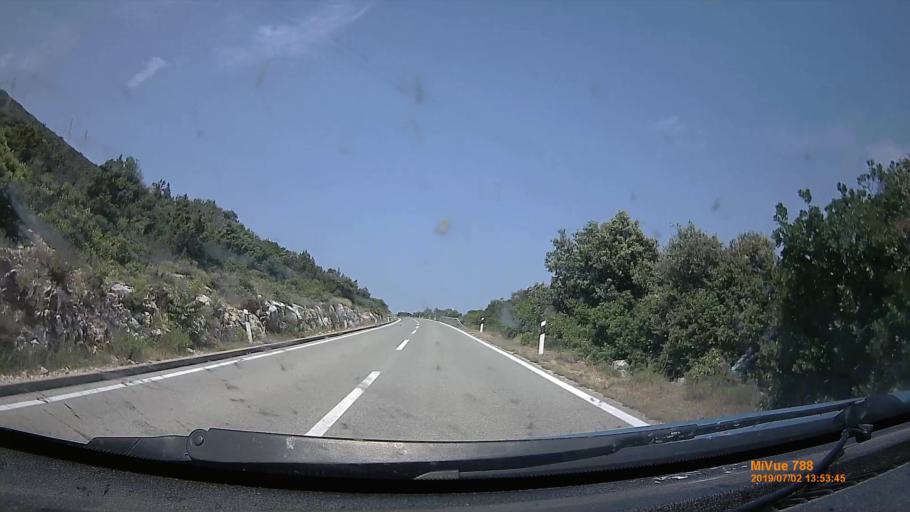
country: HR
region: Primorsko-Goranska
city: Mali Losinj
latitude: 44.6306
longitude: 14.3923
